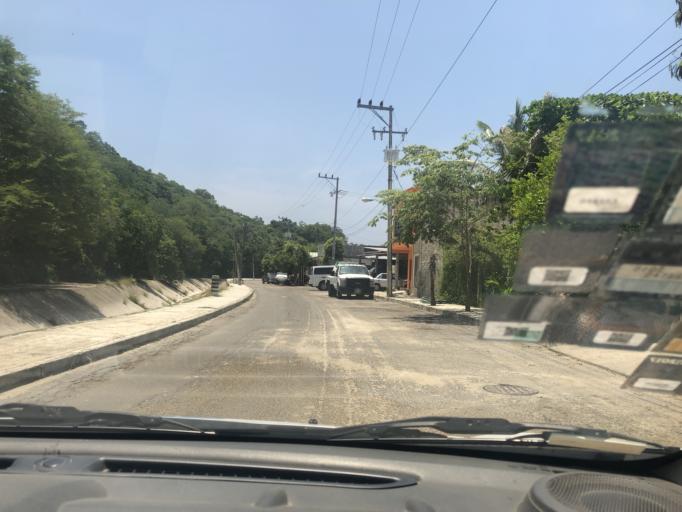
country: MX
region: Oaxaca
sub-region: Santa Maria Huatulco
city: Sector H Tres
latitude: 15.7761
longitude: -96.1482
